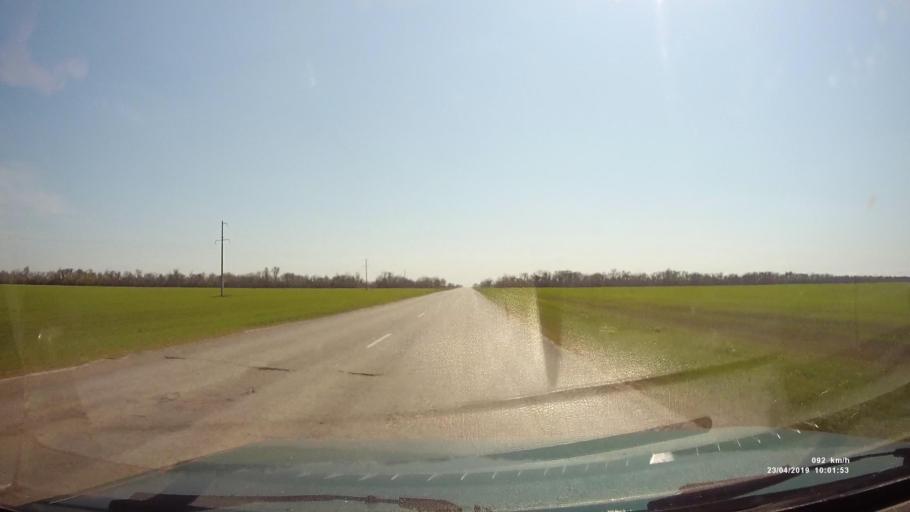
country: RU
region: Rostov
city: Sovetskoye
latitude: 46.7634
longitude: 42.1586
